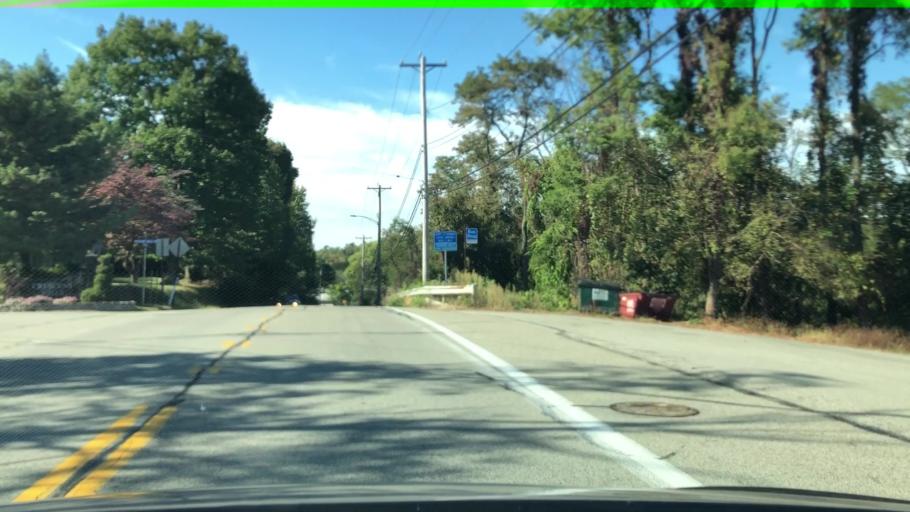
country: US
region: Pennsylvania
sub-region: Allegheny County
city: Penn Hills
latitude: 40.4729
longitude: -79.8201
